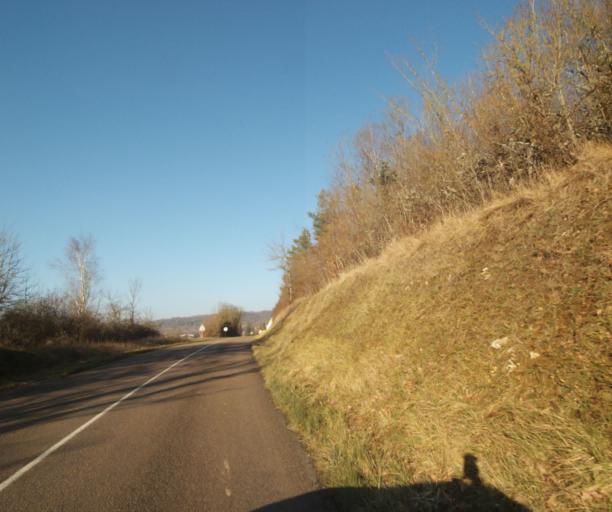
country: FR
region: Champagne-Ardenne
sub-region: Departement de la Haute-Marne
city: Chevillon
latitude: 48.5154
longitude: 5.1186
